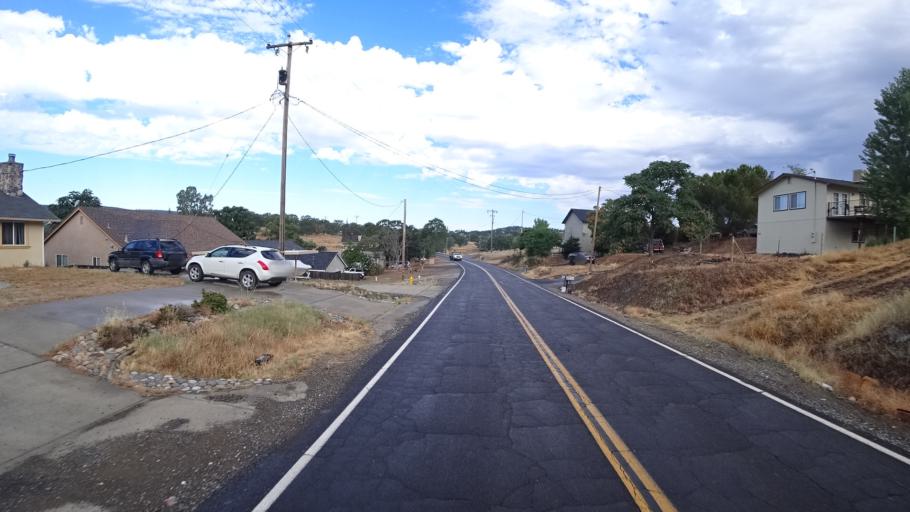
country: US
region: California
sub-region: Calaveras County
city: Copperopolis
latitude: 37.9122
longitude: -120.6171
